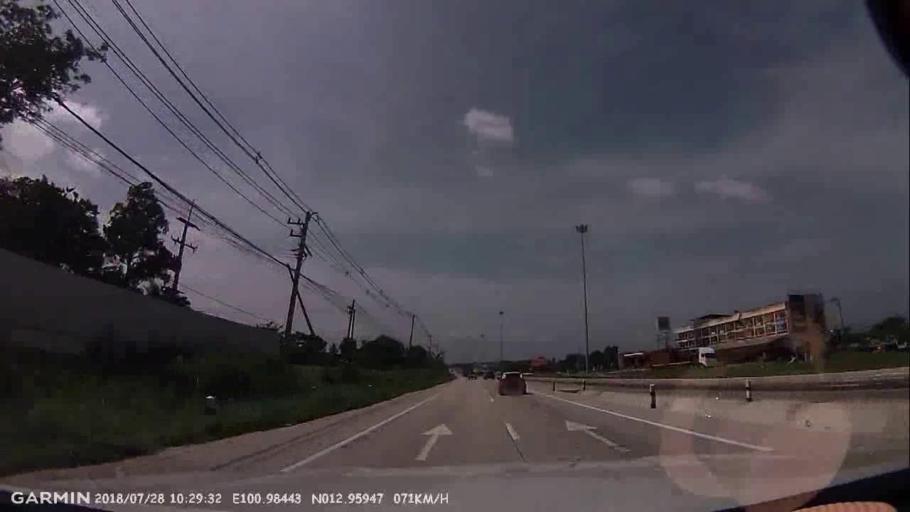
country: TH
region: Chon Buri
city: Bang Lamung
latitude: 12.9594
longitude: 100.9846
